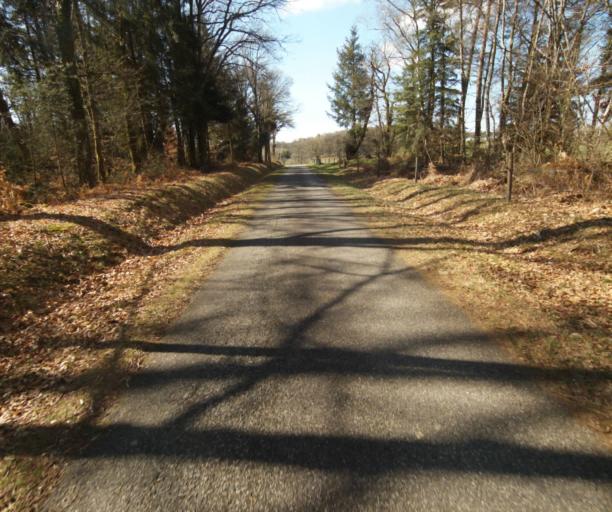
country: FR
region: Limousin
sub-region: Departement de la Correze
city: Laguenne
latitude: 45.2393
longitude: 1.9125
